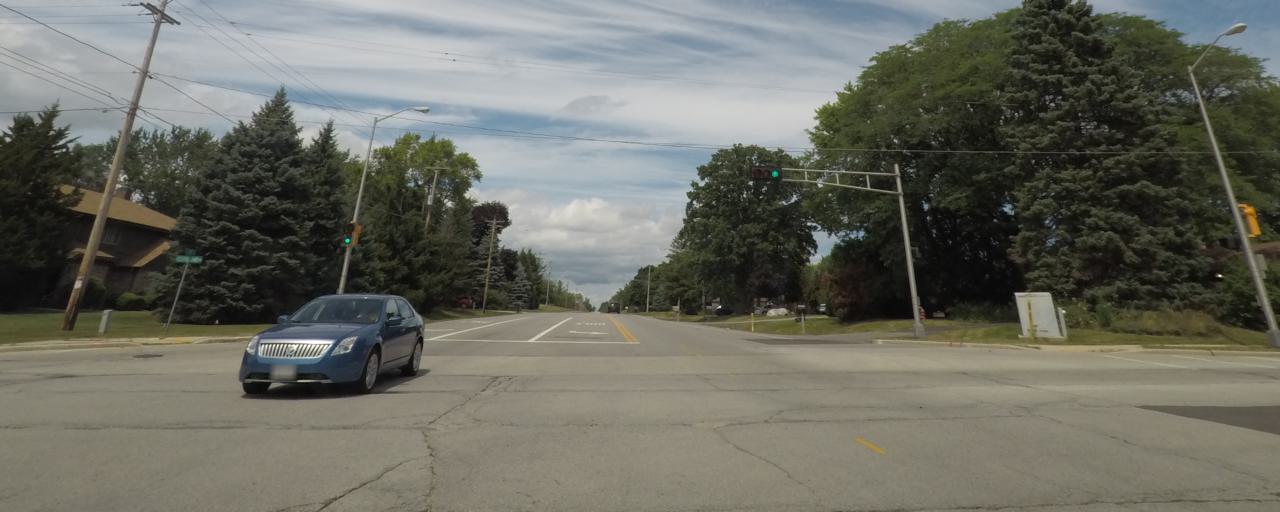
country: US
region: Wisconsin
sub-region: Waukesha County
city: New Berlin
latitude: 42.9953
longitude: -88.0680
